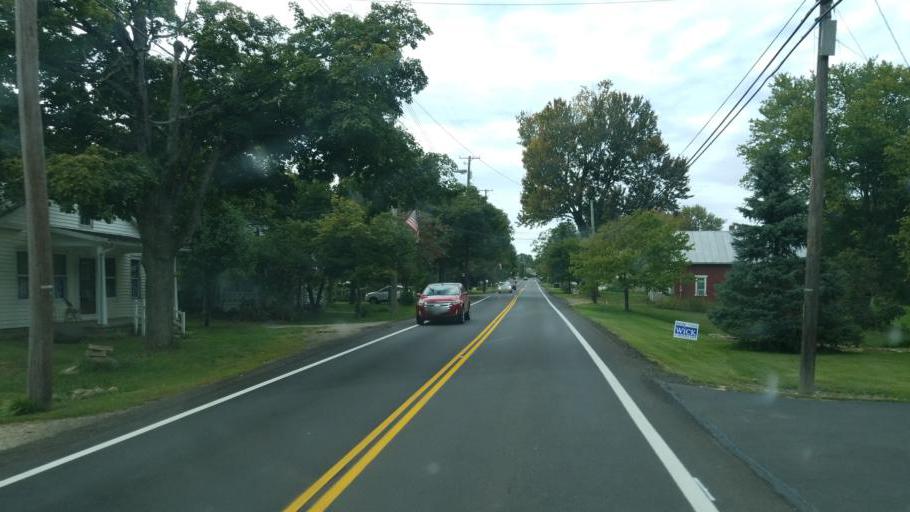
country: US
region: Ohio
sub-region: Knox County
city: Fredericktown
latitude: 40.4768
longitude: -82.6832
